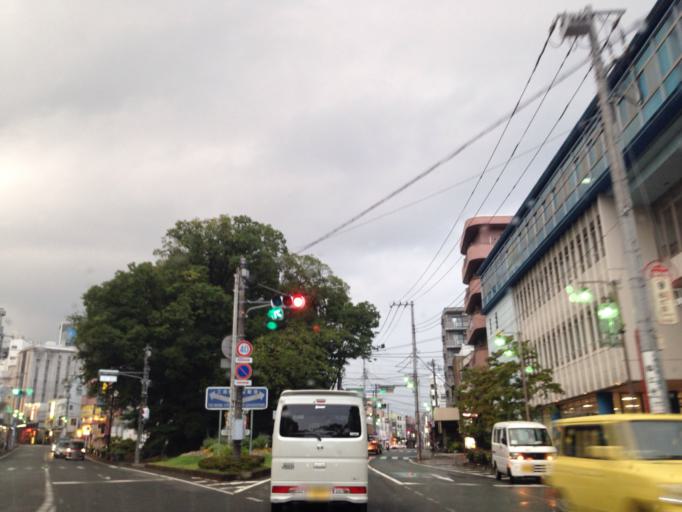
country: JP
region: Shizuoka
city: Mishima
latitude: 35.1236
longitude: 138.9140
